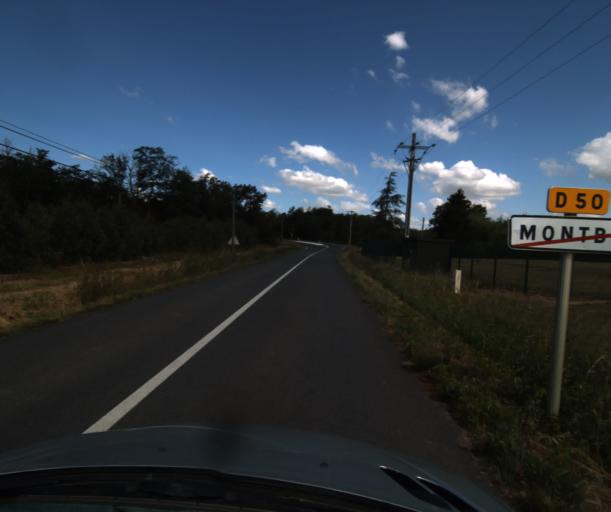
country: FR
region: Midi-Pyrenees
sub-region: Departement du Tarn-et-Garonne
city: Finhan
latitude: 43.9247
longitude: 1.2602
